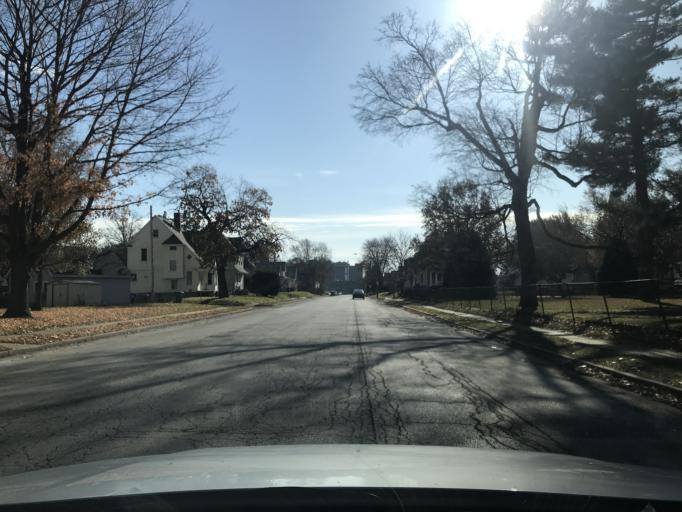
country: US
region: Iowa
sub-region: Scott County
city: Davenport
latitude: 41.5199
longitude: -90.6098
